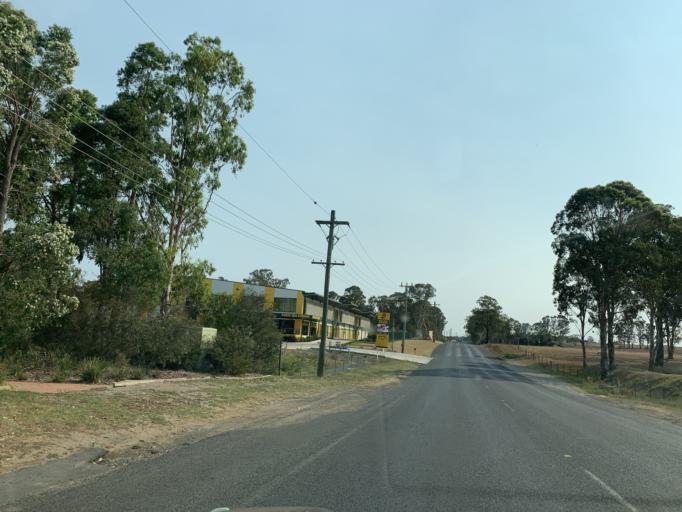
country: AU
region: New South Wales
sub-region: Blacktown
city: Rouse Hill
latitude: -33.6657
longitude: 150.9186
